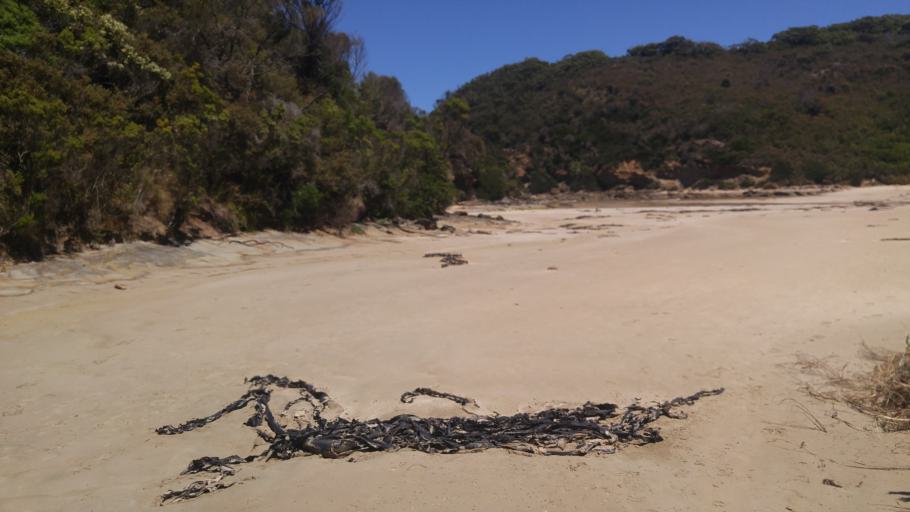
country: AU
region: Victoria
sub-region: Colac-Otway
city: Apollo Bay
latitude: -38.8444
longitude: 143.5619
